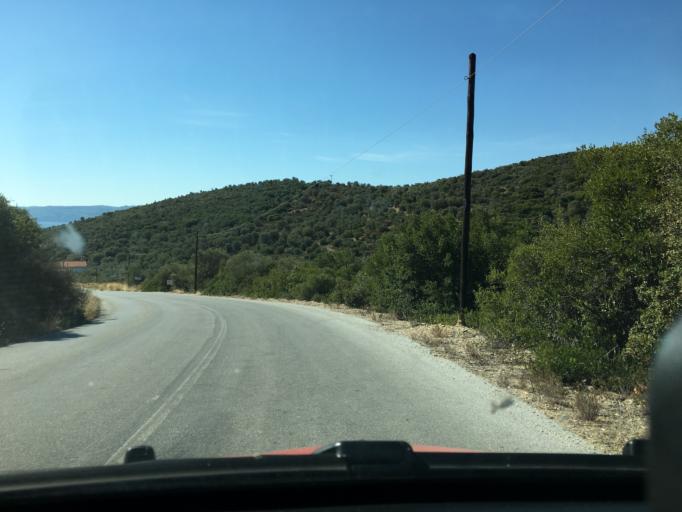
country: GR
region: Central Macedonia
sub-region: Nomos Chalkidikis
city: Agios Nikolaos
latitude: 40.3402
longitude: 23.7209
